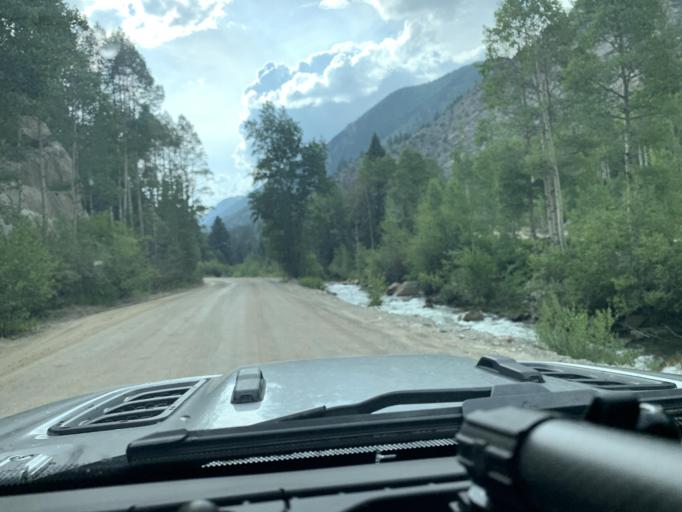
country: US
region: Colorado
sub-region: Chaffee County
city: Buena Vista
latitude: 38.7157
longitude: -106.2563
